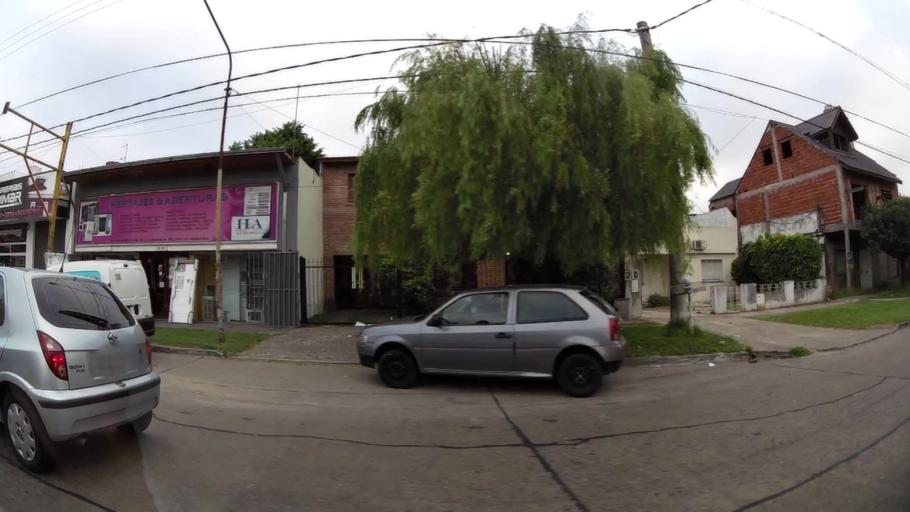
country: AR
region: Buenos Aires
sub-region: Partido de Moron
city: Moron
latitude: -34.6606
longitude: -58.5943
